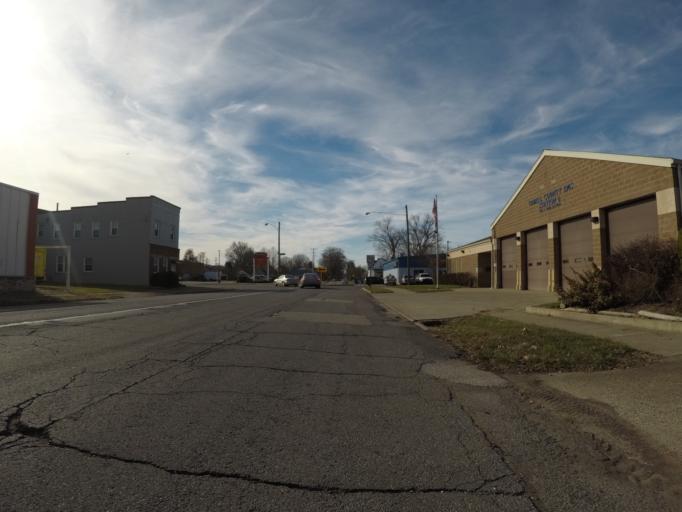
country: US
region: West Virginia
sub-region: Cabell County
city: Huntington
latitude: 38.4115
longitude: -82.4857
